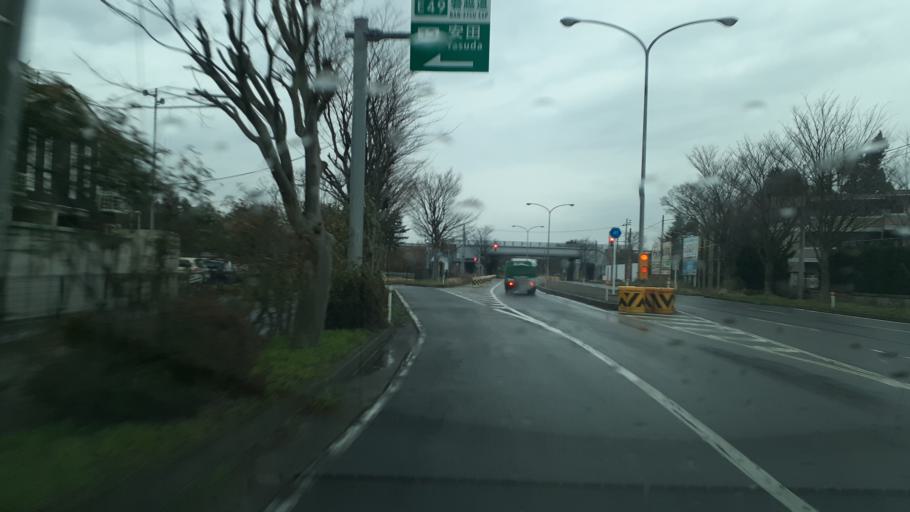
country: JP
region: Niigata
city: Gosen
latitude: 37.7608
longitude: 139.2326
